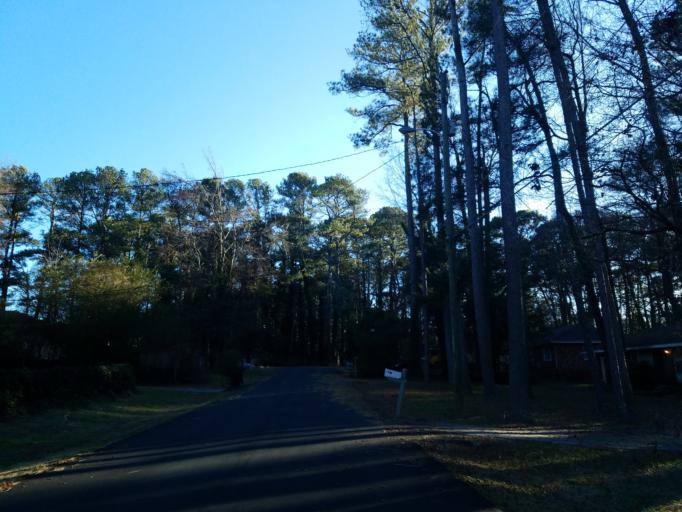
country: US
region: Georgia
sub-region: Cobb County
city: Fair Oaks
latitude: 33.9385
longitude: -84.4966
